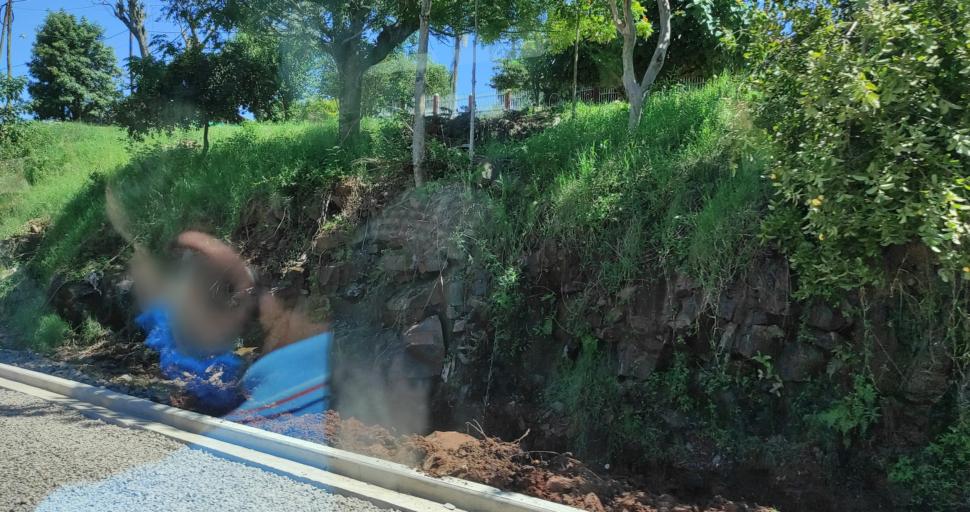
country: AR
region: Misiones
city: El Soberbio
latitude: -27.2920
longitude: -54.2057
